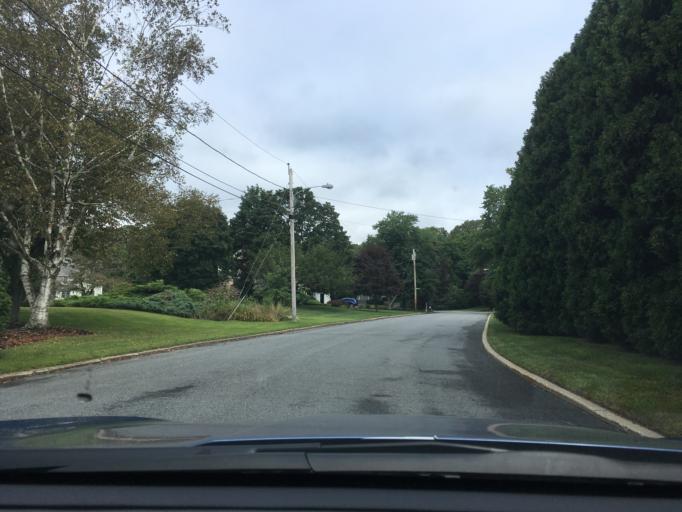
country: US
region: Rhode Island
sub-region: Kent County
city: East Greenwich
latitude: 41.6609
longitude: -71.4853
